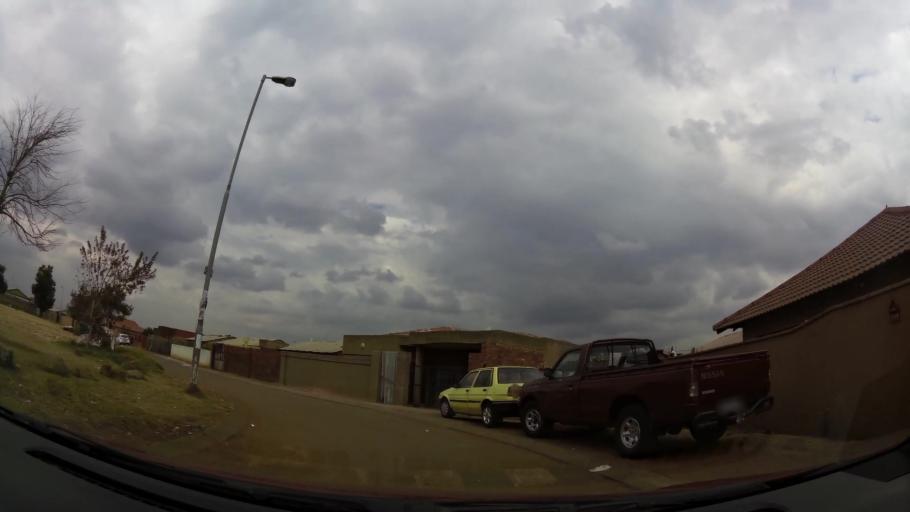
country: ZA
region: Gauteng
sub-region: City of Johannesburg Metropolitan Municipality
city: Soweto
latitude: -26.2524
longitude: 27.8511
